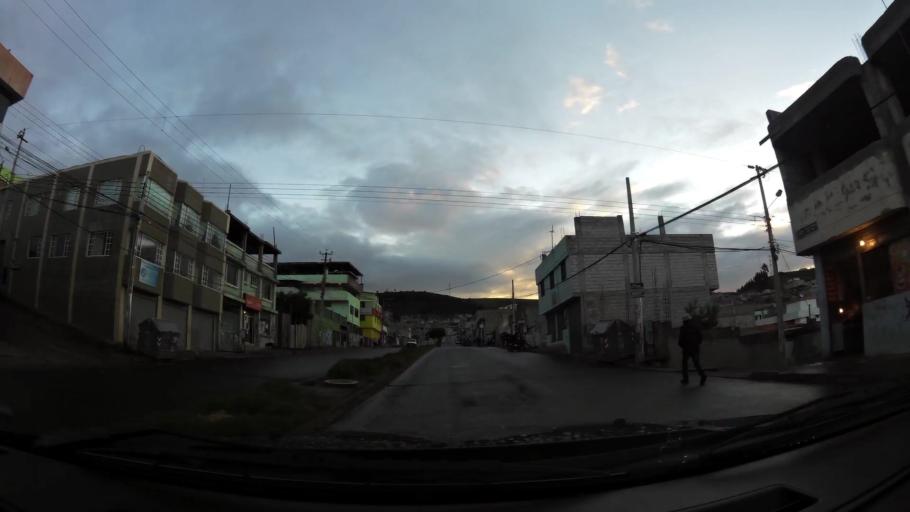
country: EC
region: Pichincha
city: Quito
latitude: -0.0909
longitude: -78.5226
